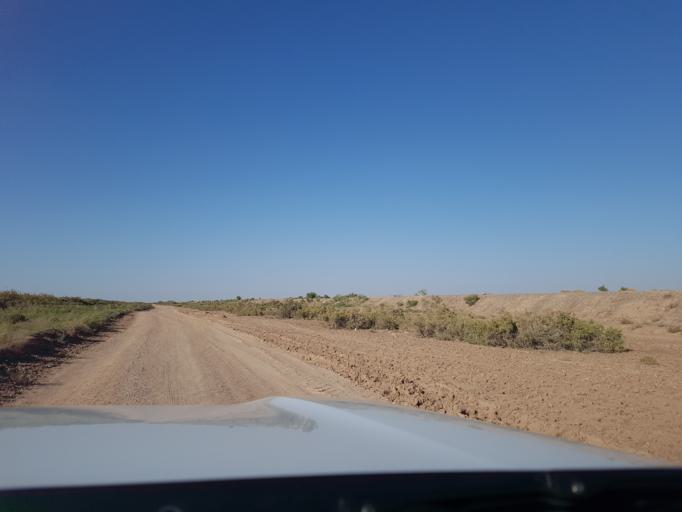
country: IR
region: Razavi Khorasan
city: Sarakhs
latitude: 36.9738
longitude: 61.3844
